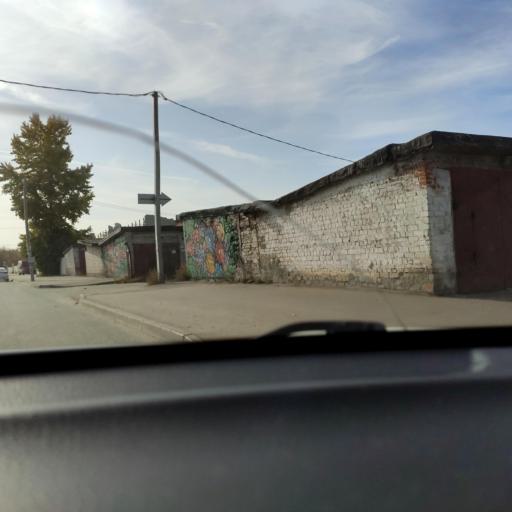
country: RU
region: Tatarstan
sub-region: Gorod Kazan'
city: Kazan
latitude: 55.8060
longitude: 49.0617
